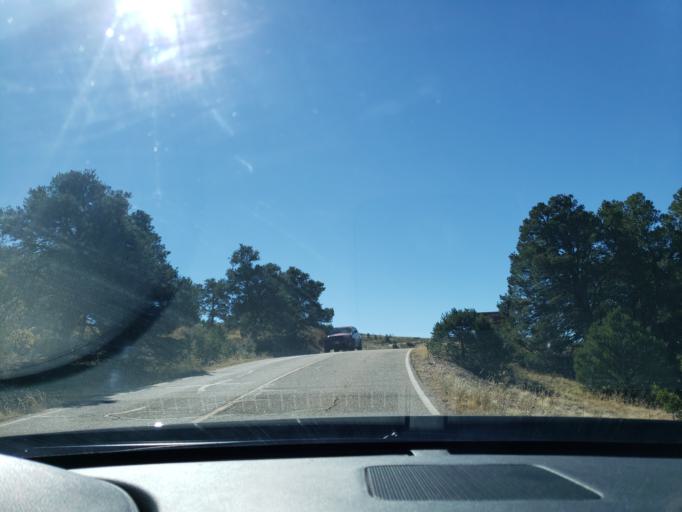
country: US
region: Colorado
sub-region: Fremont County
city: Canon City
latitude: 38.4737
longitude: -105.3075
